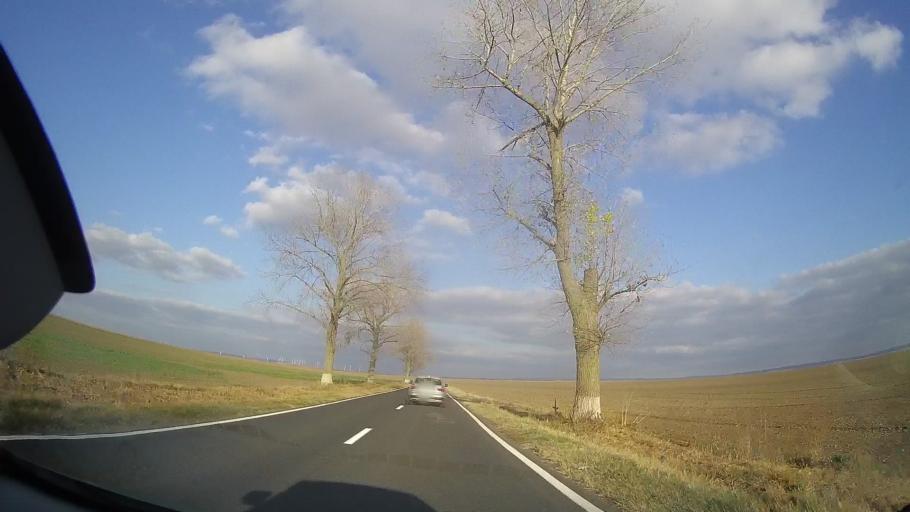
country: RO
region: Tulcea
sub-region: Comuna Topolog
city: Topolog
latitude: 44.8263
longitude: 28.2753
